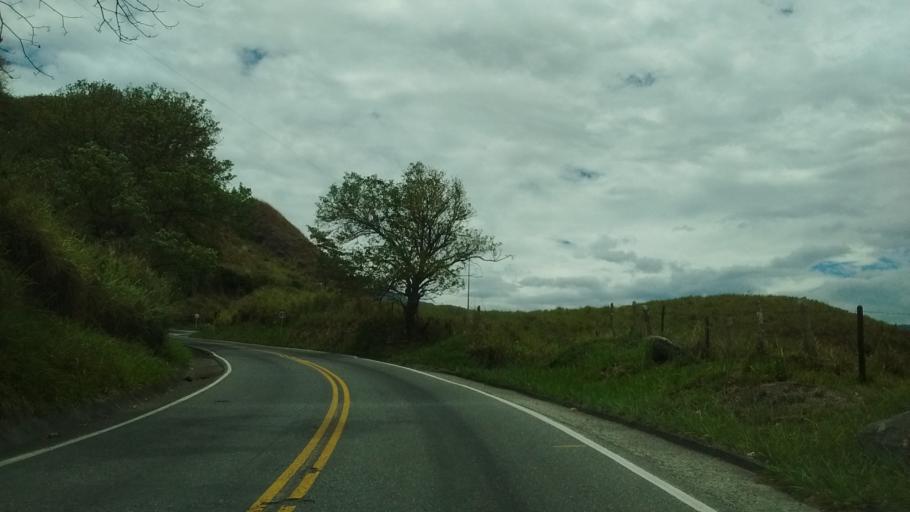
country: CO
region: Cauca
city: La Sierra
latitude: 2.2074
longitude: -76.8012
